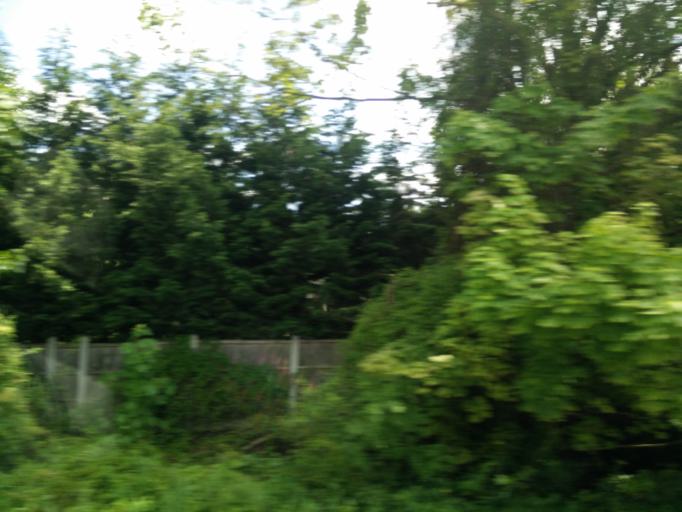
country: GB
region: England
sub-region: Cambridgeshire
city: Harston
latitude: 52.1461
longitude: 0.0905
